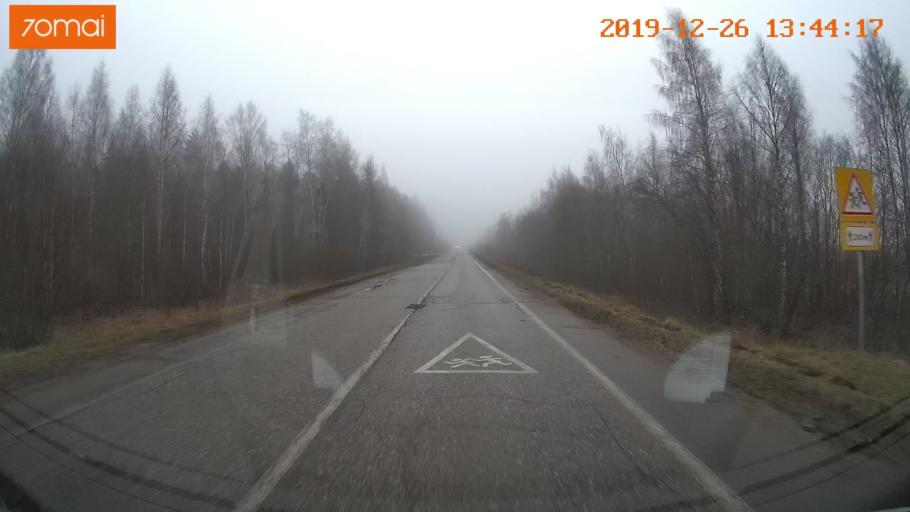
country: RU
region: Vologda
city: Sheksna
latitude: 58.7032
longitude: 38.5043
